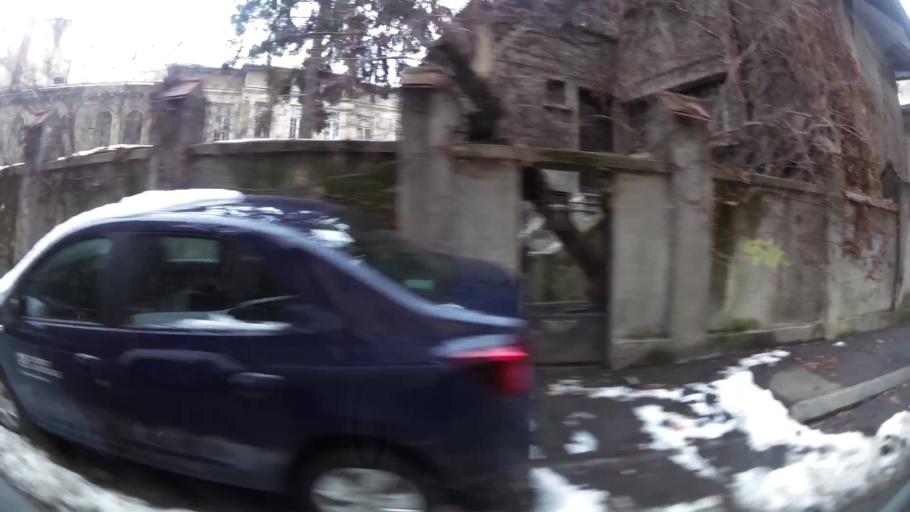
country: RO
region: Bucuresti
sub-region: Municipiul Bucuresti
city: Bucharest
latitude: 44.4404
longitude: 26.1100
